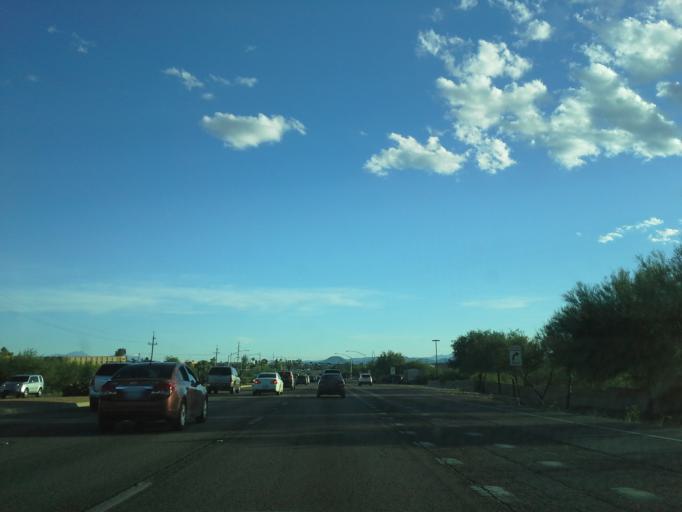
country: US
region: Arizona
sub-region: Pima County
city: Casas Adobes
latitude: 32.3476
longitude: -110.9759
